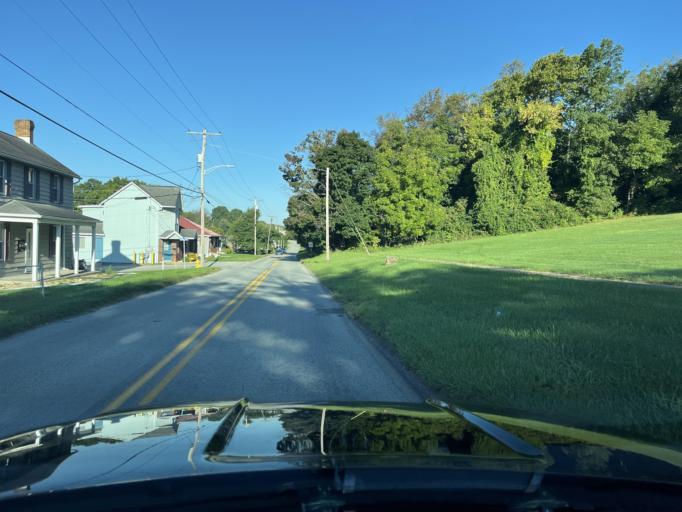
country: US
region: Pennsylvania
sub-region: Fayette County
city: Leith-Hatfield
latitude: 39.8790
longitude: -79.7286
